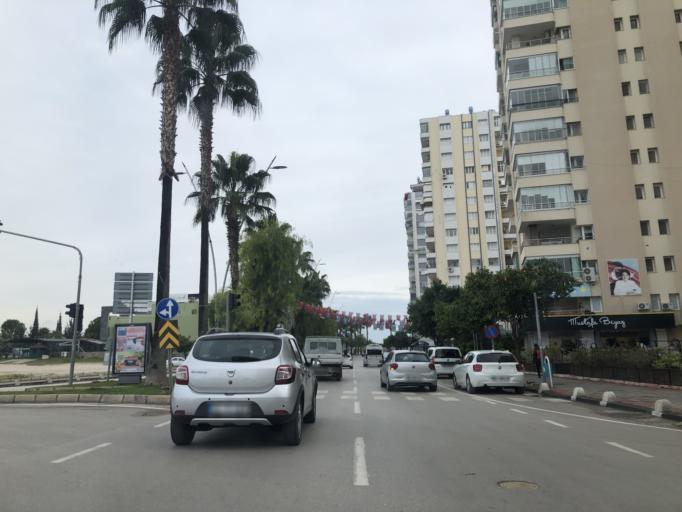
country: TR
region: Adana
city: Adana
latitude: 37.0566
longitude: 35.2831
